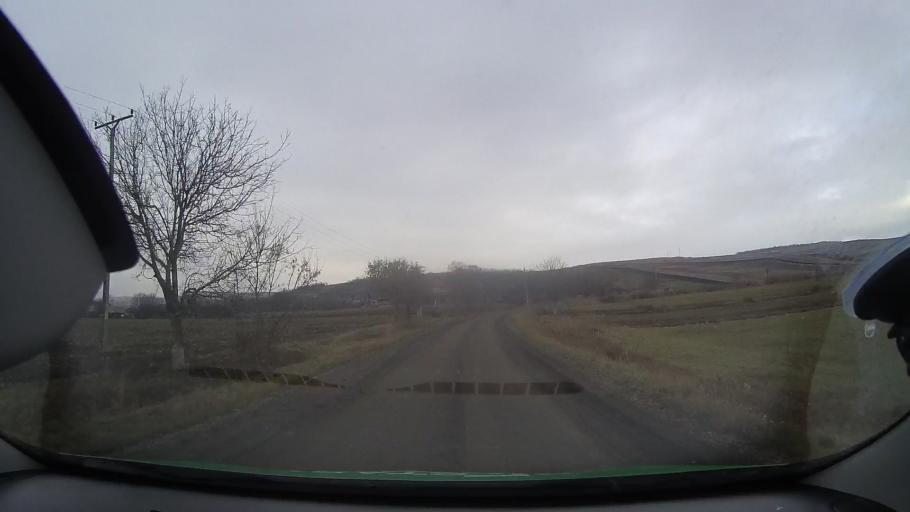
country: RO
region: Mures
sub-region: Comuna Bichis
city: Bichis
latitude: 46.3826
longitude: 24.0814
